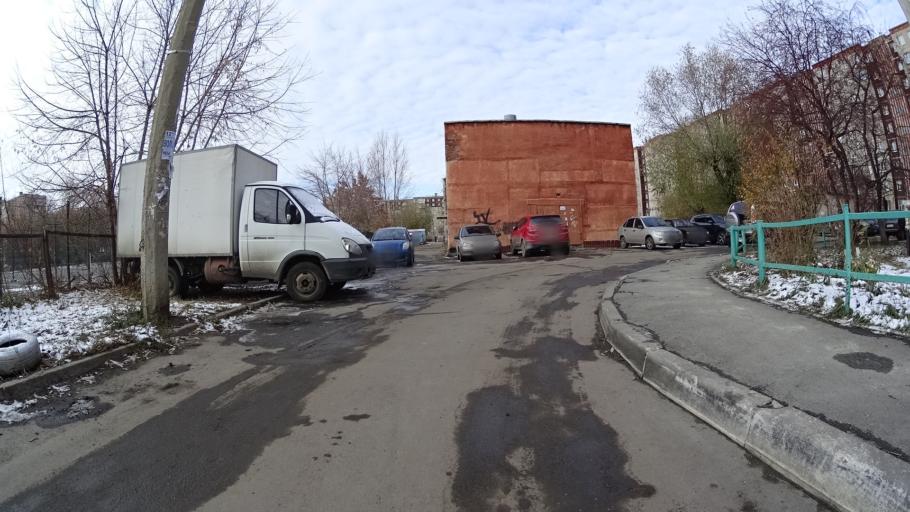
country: RU
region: Chelyabinsk
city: Roshchino
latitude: 55.1894
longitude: 61.2996
